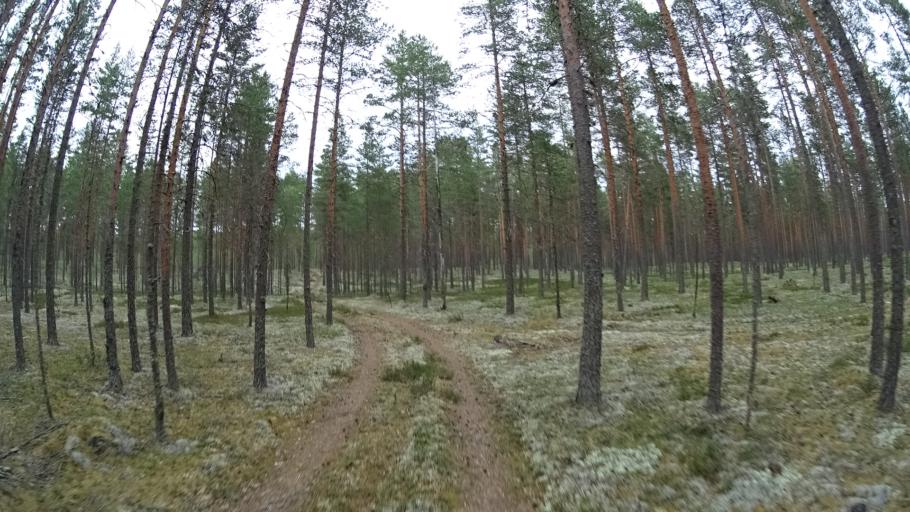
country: FI
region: Satakunta
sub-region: Pohjois-Satakunta
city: Jaemijaervi
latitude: 61.7626
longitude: 22.7598
